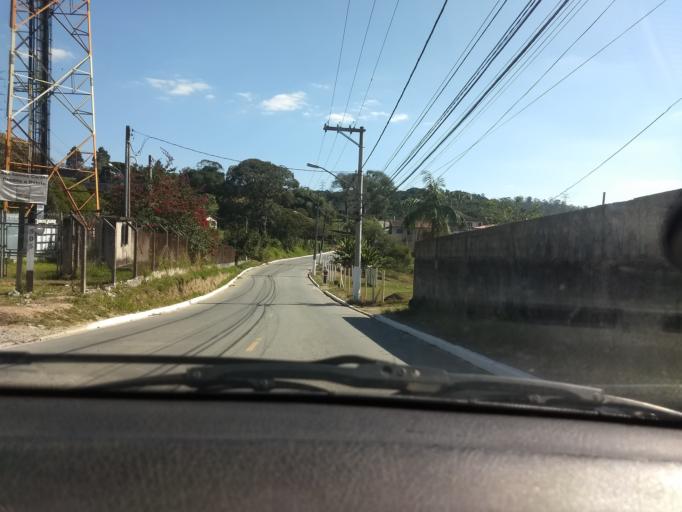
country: BR
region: Sao Paulo
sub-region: Embu-Guacu
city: Embu Guacu
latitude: -23.8028
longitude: -46.7372
